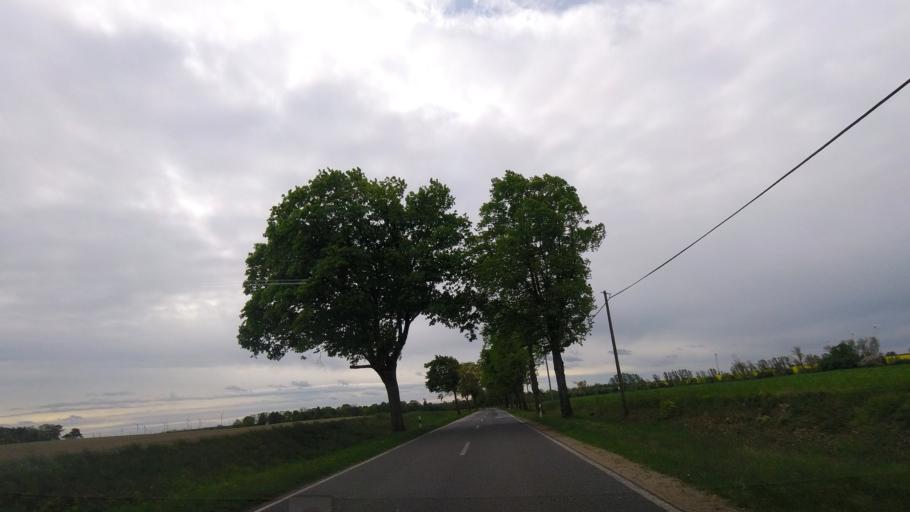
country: DE
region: Brandenburg
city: Dahme
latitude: 51.8929
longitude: 13.4133
